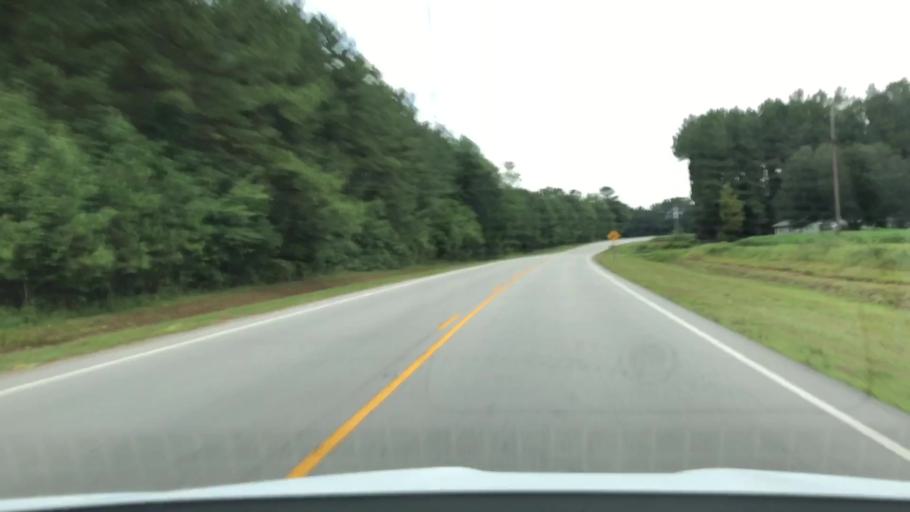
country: US
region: North Carolina
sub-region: Jones County
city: Trenton
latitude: 35.0383
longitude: -77.3468
